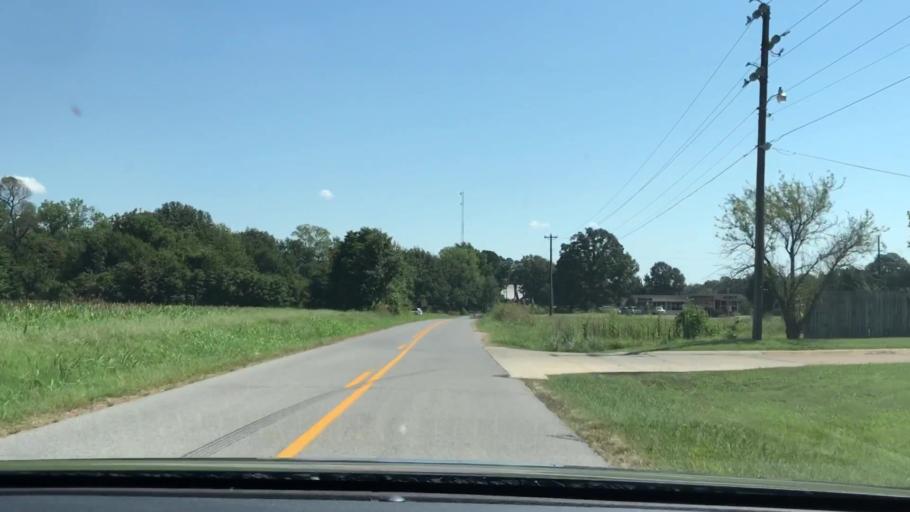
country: US
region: Kentucky
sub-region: Fulton County
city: Fulton
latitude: 36.5211
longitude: -88.8916
